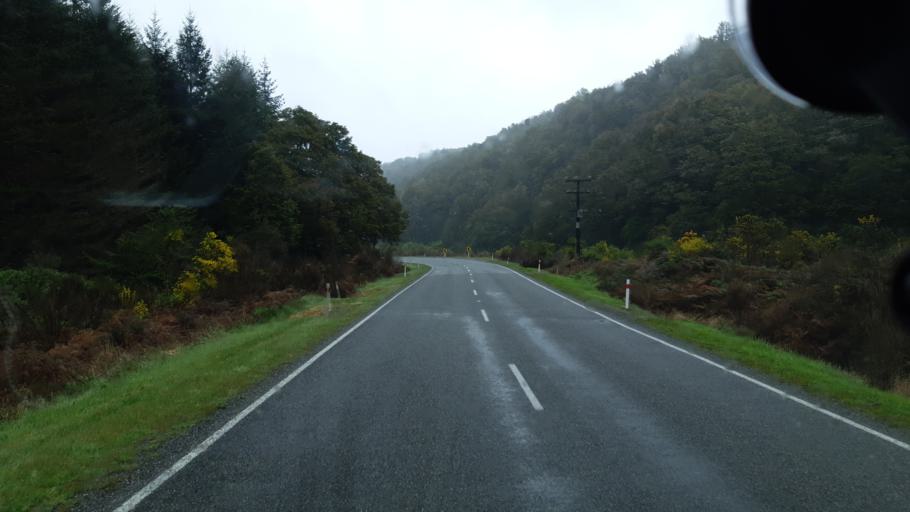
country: NZ
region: West Coast
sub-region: Buller District
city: Westport
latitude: -42.1499
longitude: 171.7853
